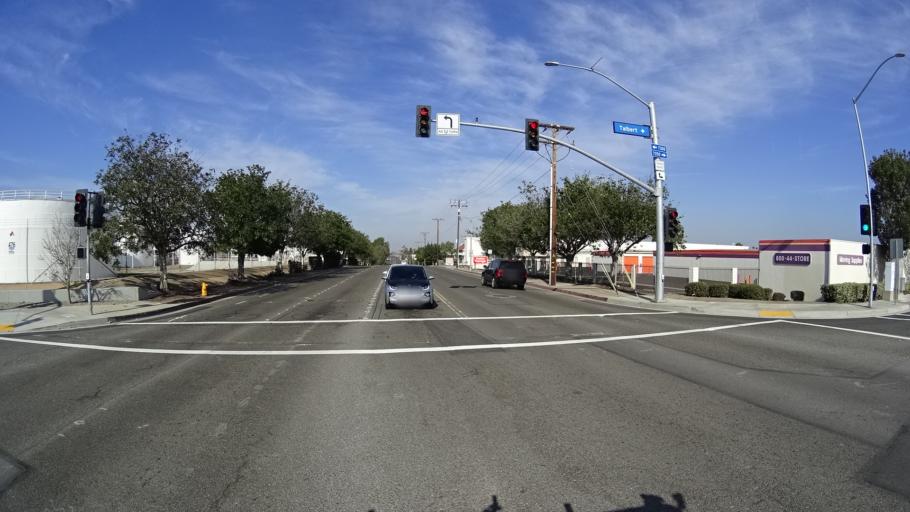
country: US
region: California
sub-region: Orange County
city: Huntington Beach
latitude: 33.7012
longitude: -117.9998
